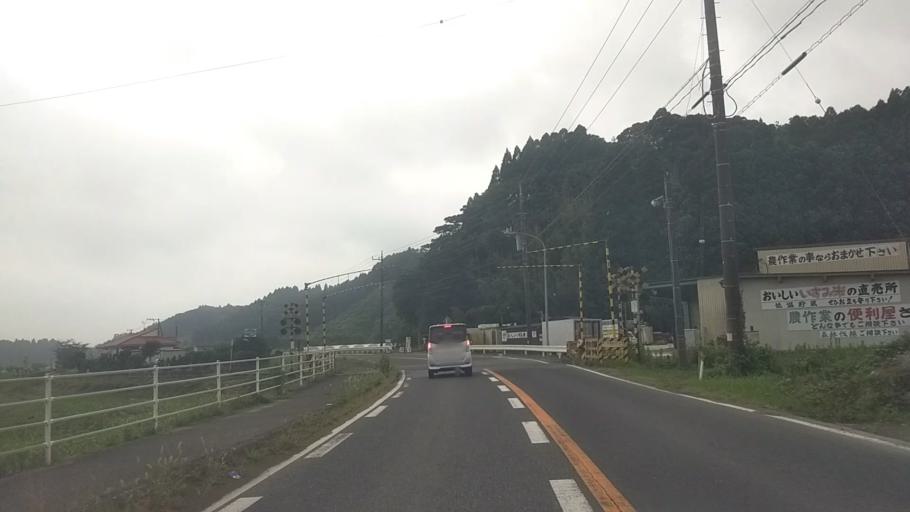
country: JP
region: Chiba
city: Ohara
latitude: 35.2783
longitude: 140.3263
